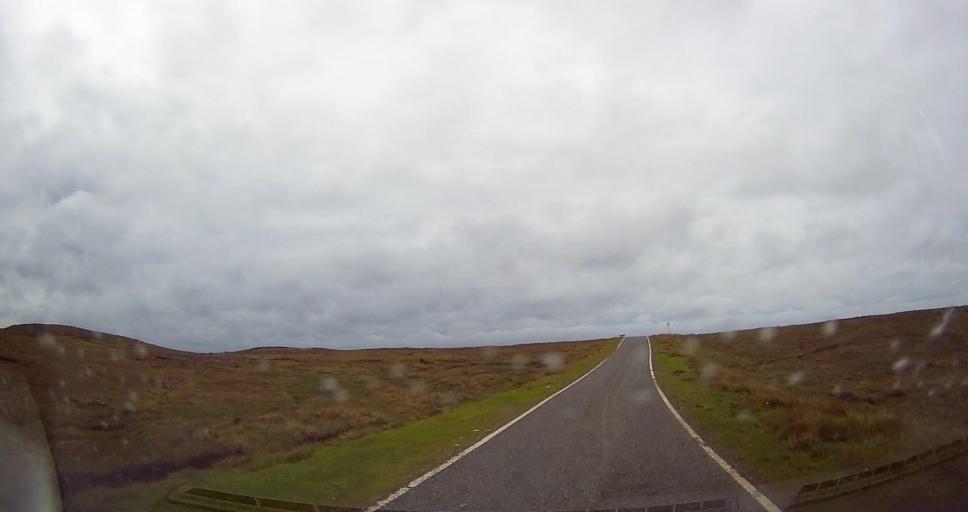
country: GB
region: Scotland
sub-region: Shetland Islands
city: Lerwick
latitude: 60.4923
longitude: -1.5712
